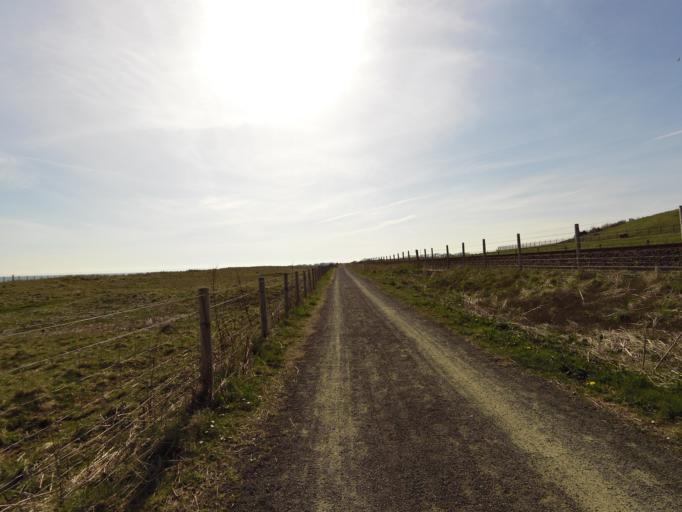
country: GB
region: Scotland
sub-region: Angus
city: Carnoustie
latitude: 56.5245
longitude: -2.6454
